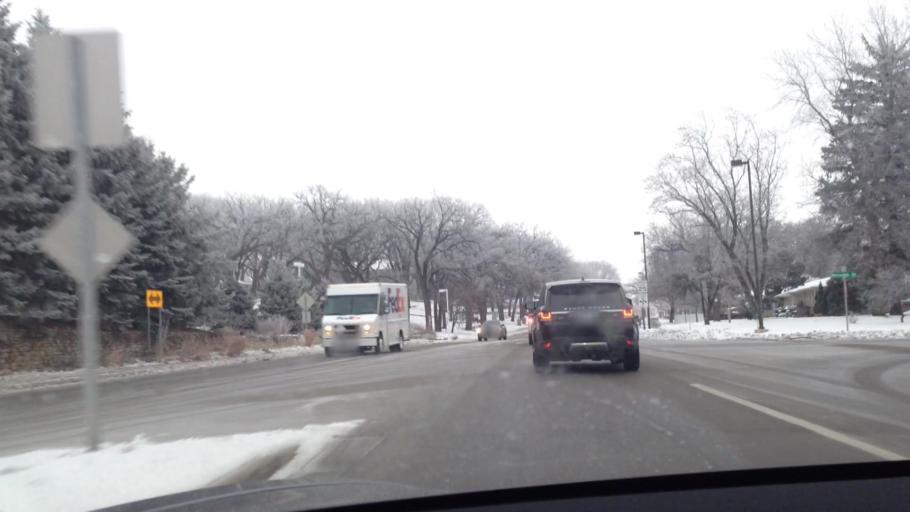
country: US
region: Minnesota
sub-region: Hennepin County
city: Edina
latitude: 44.8763
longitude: -93.3489
